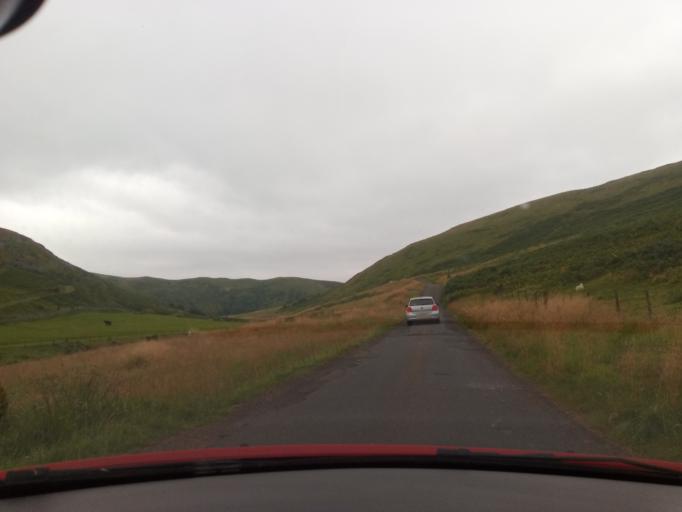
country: GB
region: England
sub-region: Northumberland
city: Rochester
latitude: 55.3627
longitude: -2.1817
